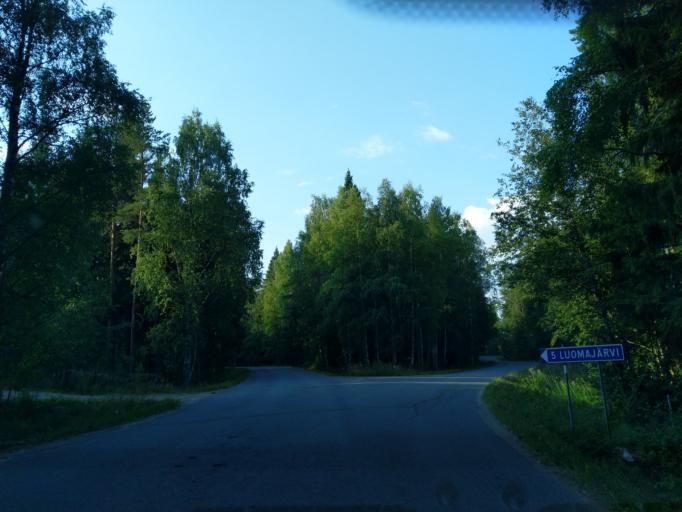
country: FI
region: Satakunta
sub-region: Pori
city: Laengelmaeki
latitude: 61.8116
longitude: 22.1908
